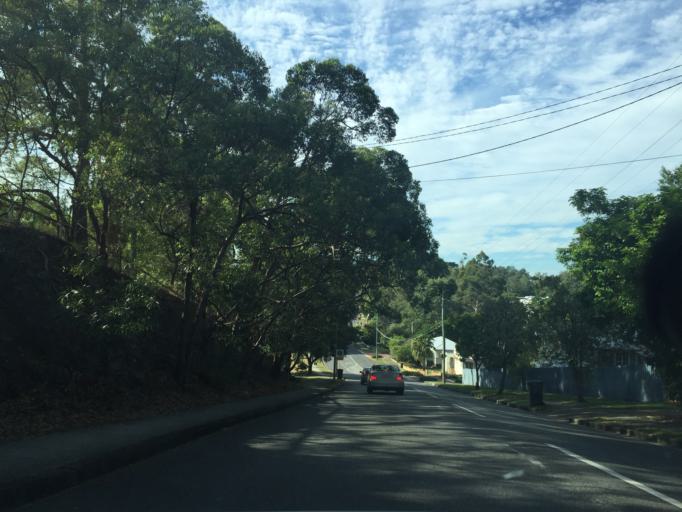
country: AU
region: Queensland
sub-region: Brisbane
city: Milton
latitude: -27.4507
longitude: 152.9778
